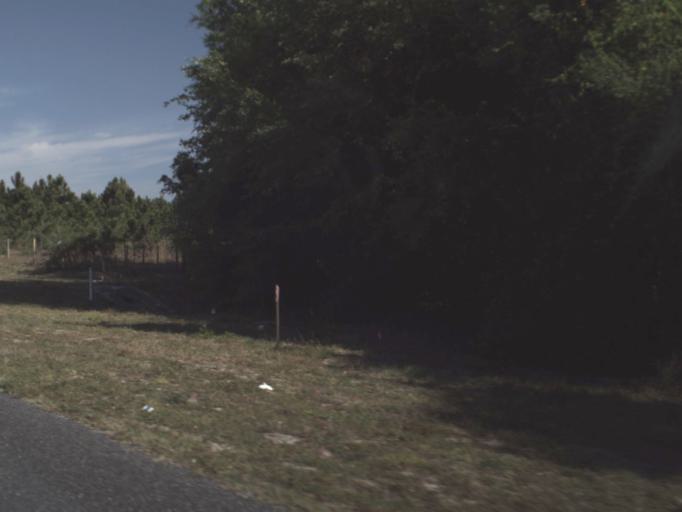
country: US
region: Florida
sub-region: Lake County
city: Hawthorne
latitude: 28.7391
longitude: -81.8718
